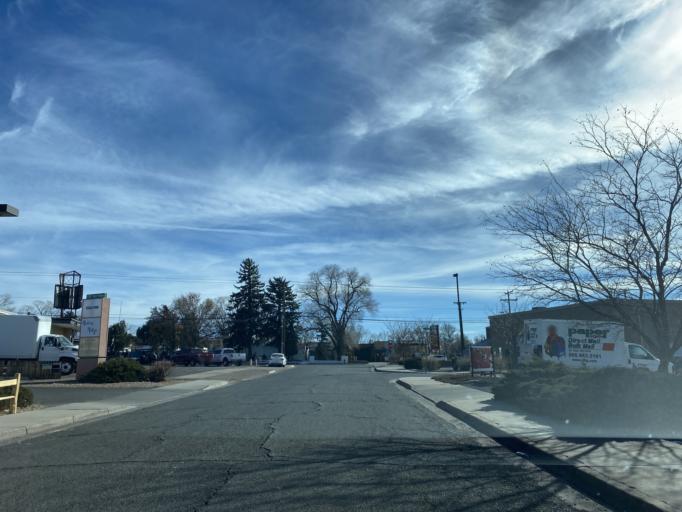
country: US
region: New Mexico
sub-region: Santa Fe County
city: Santa Fe
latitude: 35.6649
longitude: -105.9745
